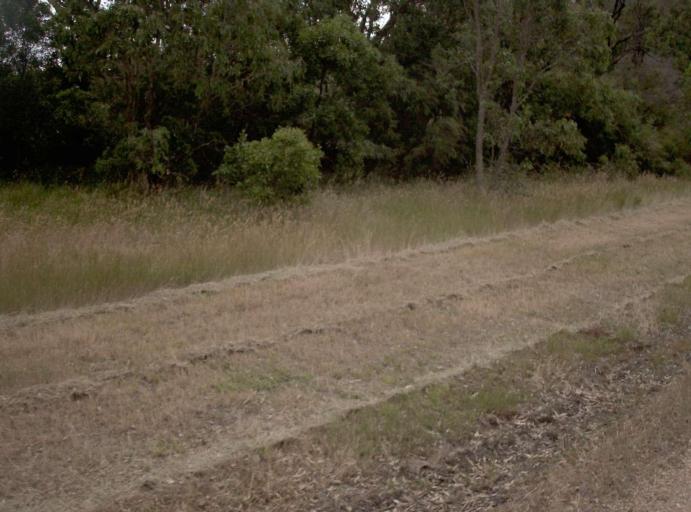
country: AU
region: Victoria
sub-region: Wellington
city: Sale
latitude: -38.0004
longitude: 147.3264
